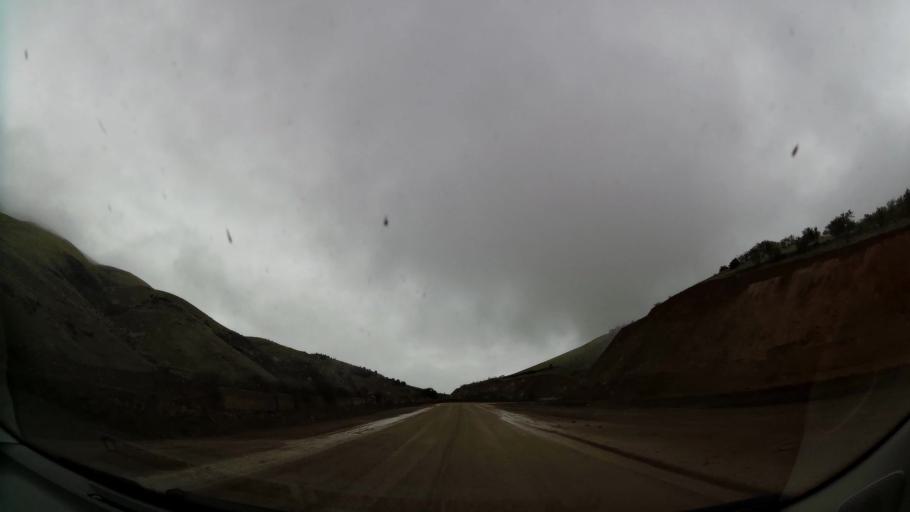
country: MA
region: Taza-Al Hoceima-Taounate
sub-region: Taza
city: Ajdir
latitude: 34.9082
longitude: -3.7957
